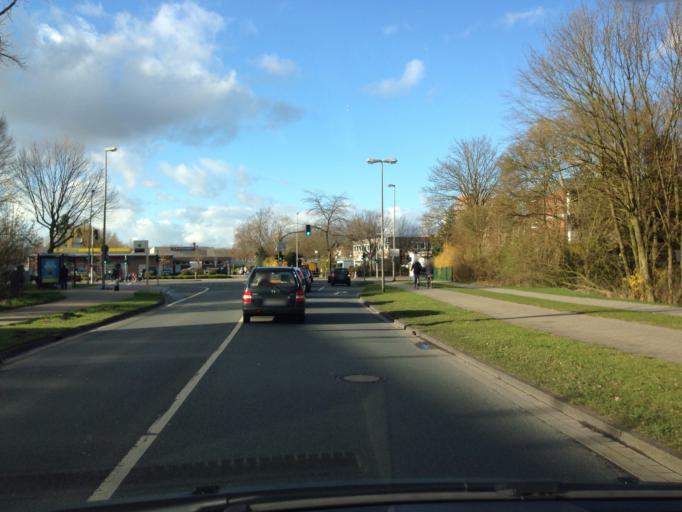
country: DE
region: North Rhine-Westphalia
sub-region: Regierungsbezirk Munster
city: Muenster
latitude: 51.9921
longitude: 7.6483
